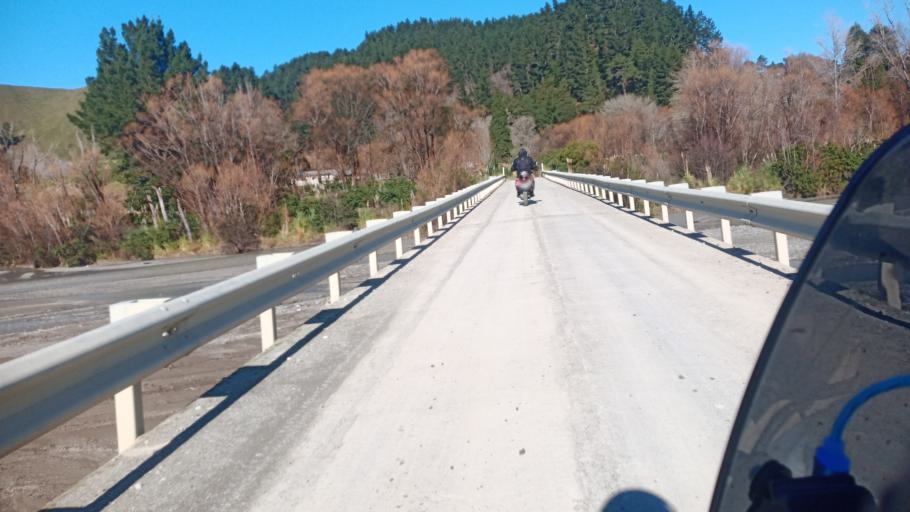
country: NZ
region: Gisborne
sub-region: Gisborne District
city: Gisborne
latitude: -38.2828
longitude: 177.8505
